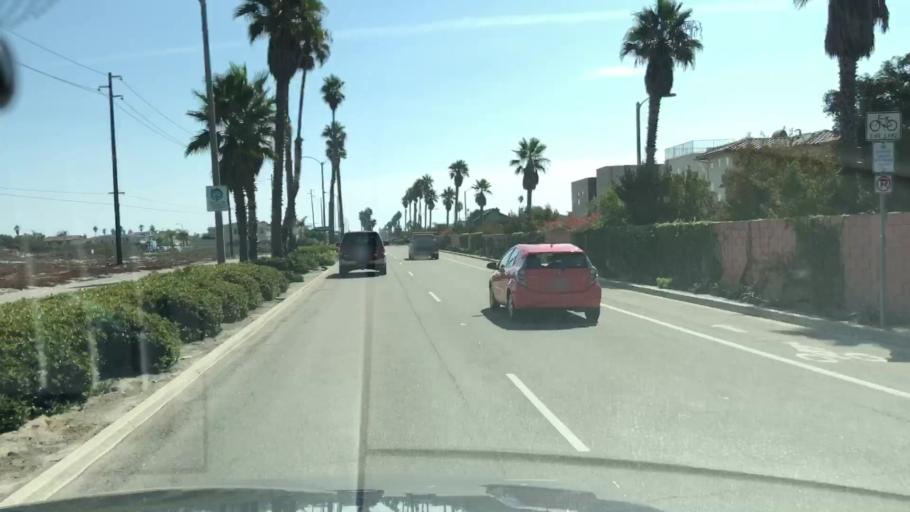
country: US
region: California
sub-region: Ventura County
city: Oxnard Shores
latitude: 34.1959
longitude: -119.2415
